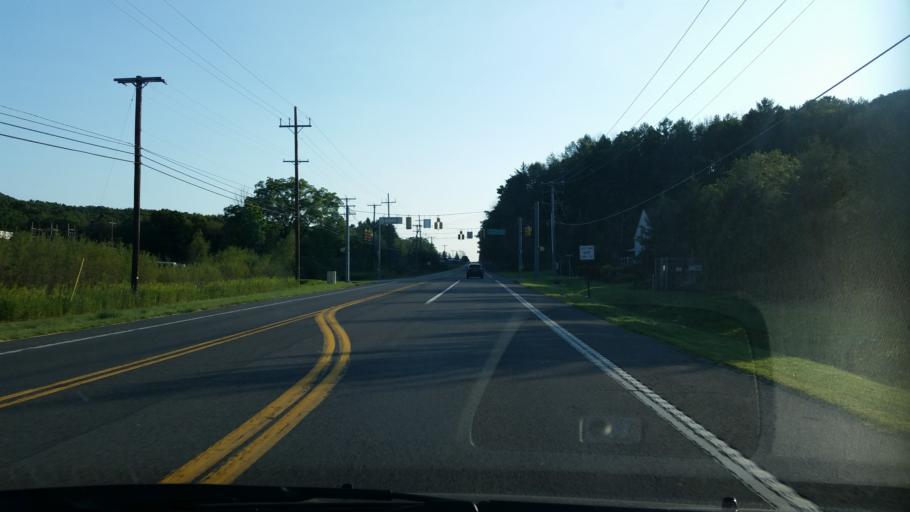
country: US
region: Pennsylvania
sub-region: Blair County
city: Tipton
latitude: 40.6233
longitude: -78.2997
